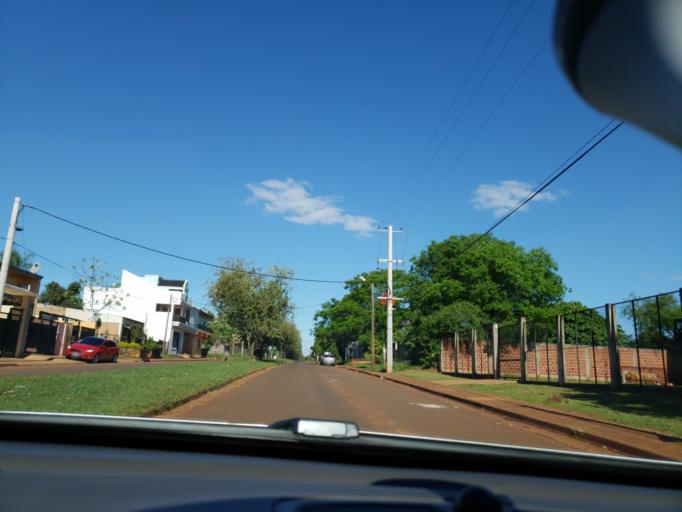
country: AR
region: Misiones
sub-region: Departamento de Capital
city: Posadas
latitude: -27.3824
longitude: -55.9481
